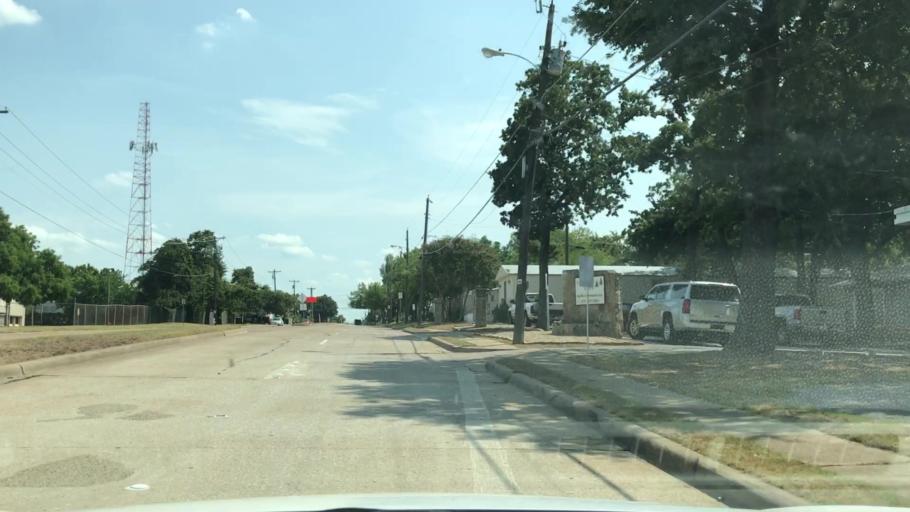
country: US
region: Texas
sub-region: Dallas County
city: Irving
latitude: 32.8334
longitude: -96.9076
